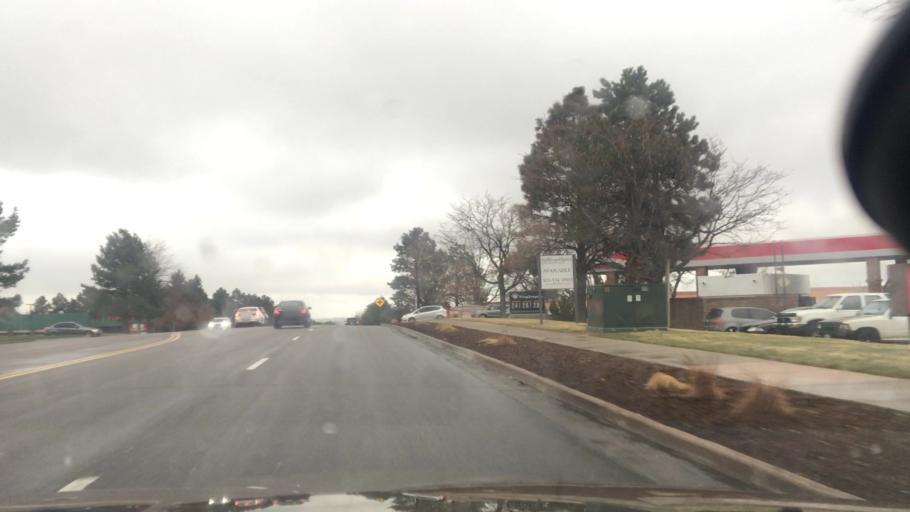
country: US
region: Colorado
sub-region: Arapahoe County
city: Castlewood
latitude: 39.5667
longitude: -104.9230
